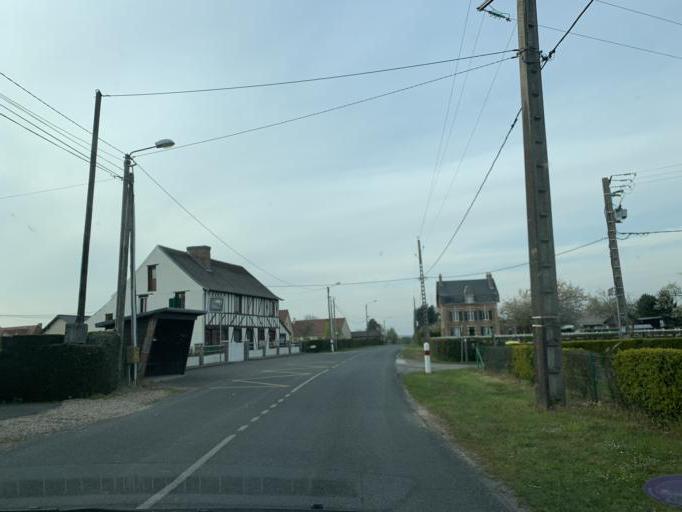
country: FR
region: Haute-Normandie
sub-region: Departement de la Seine-Maritime
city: La Mailleraye-sur-Seine
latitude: 49.4660
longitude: 0.7784
